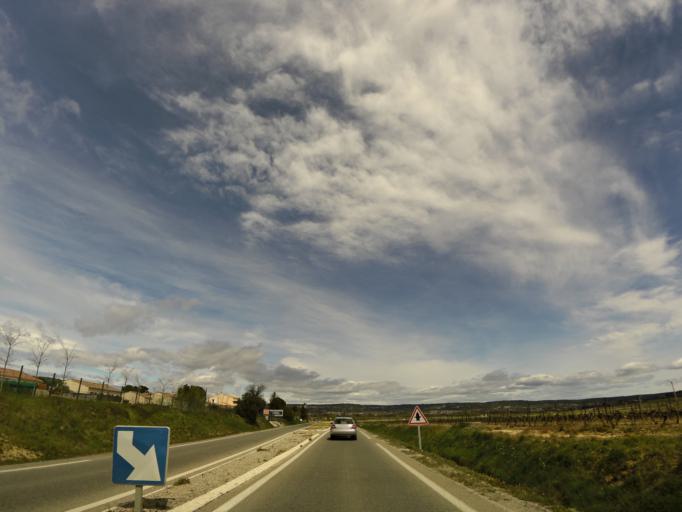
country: FR
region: Languedoc-Roussillon
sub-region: Departement du Gard
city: Calvisson
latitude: 43.7895
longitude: 4.2058
